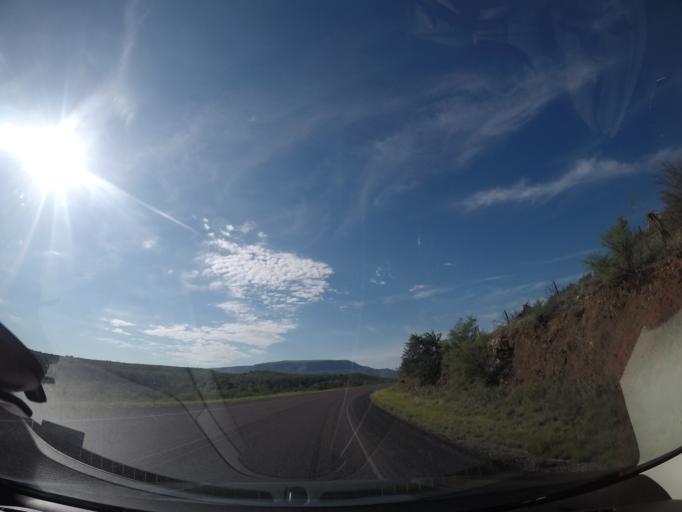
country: US
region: Texas
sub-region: Brewster County
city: Alpine
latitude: 30.0666
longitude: -103.5850
